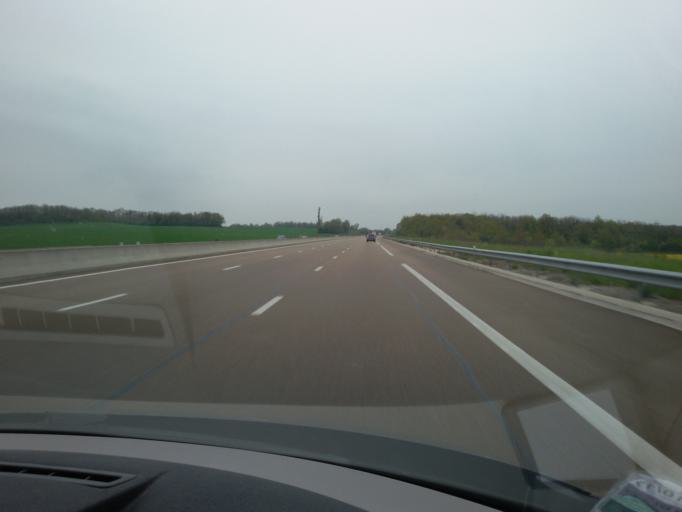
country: FR
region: Bourgogne
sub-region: Departement de la Cote-d'Or
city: Saint-Julien
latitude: 47.4553
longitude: 5.1742
